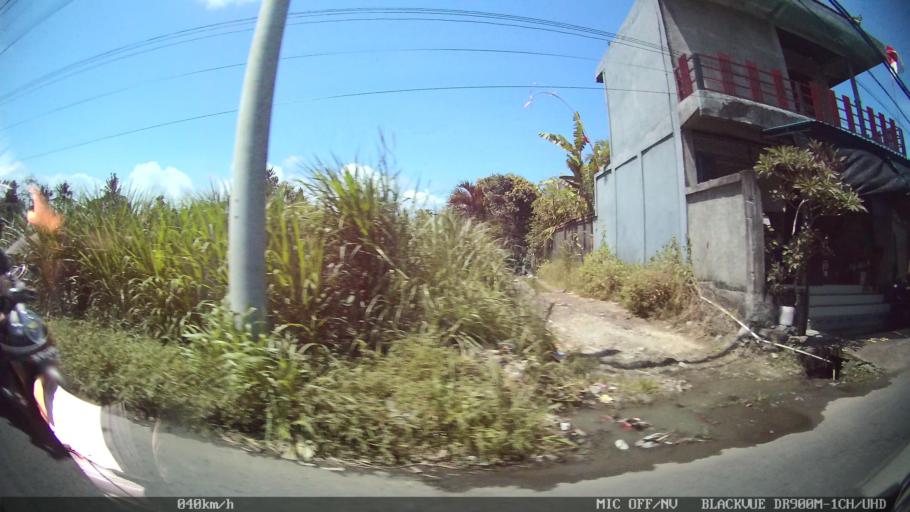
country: ID
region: Bali
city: Klungkung
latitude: -8.5594
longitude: 115.3379
